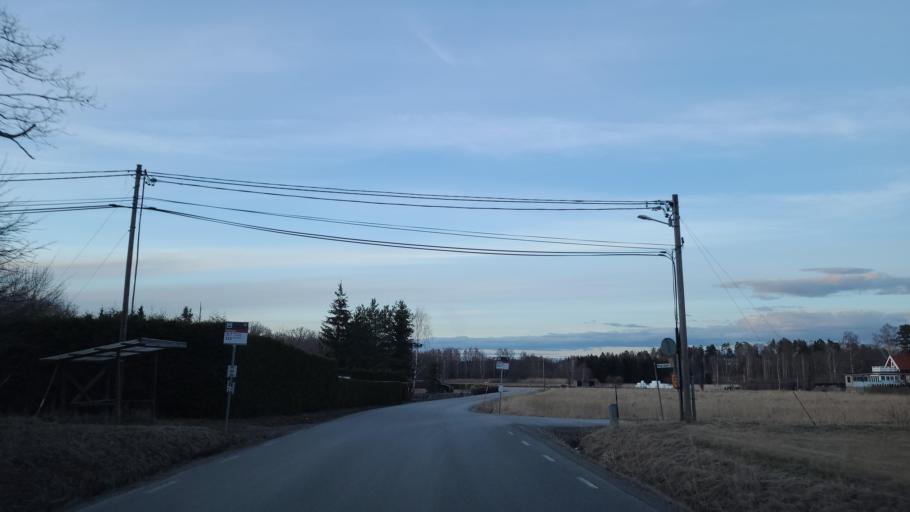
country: SE
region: Stockholm
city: Stenhamra
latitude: 59.4094
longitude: 17.6618
